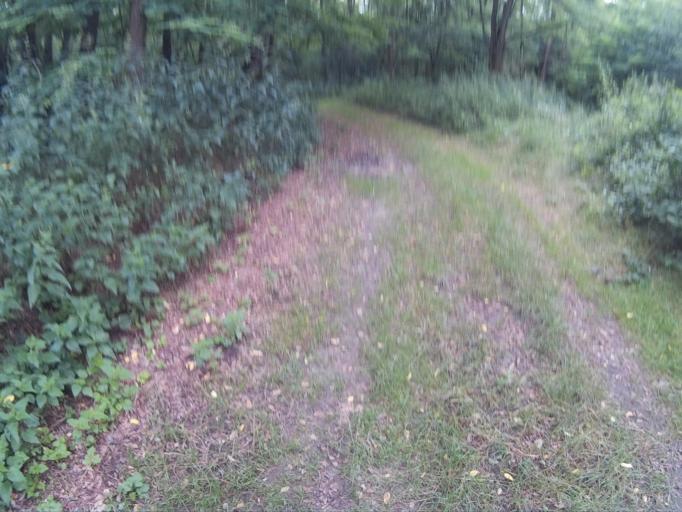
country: HU
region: Veszprem
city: Papa
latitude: 47.2788
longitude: 17.5682
